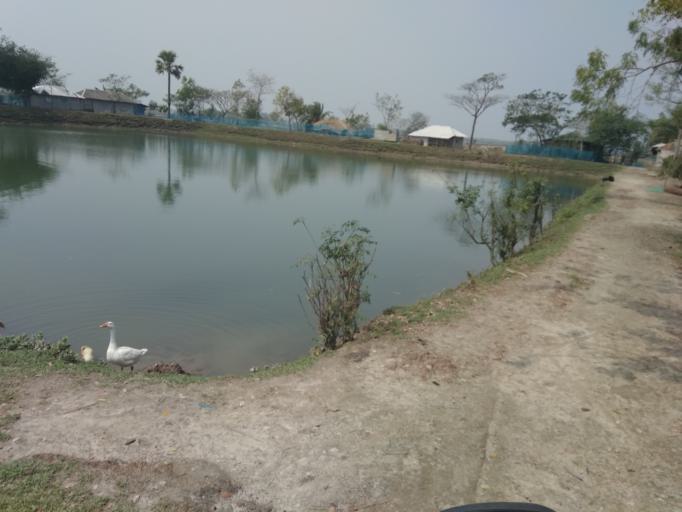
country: IN
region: West Bengal
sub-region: North 24 Parganas
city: Taki
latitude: 22.2599
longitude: 89.2589
